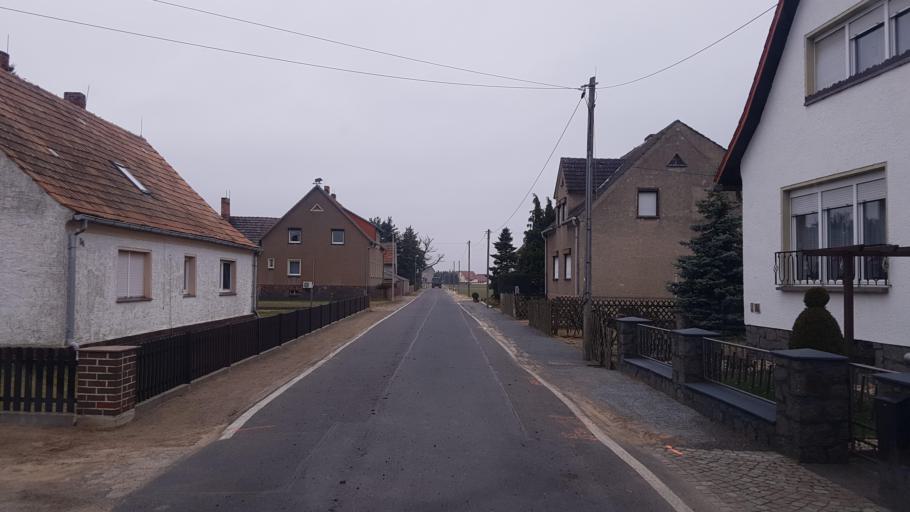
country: DE
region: Brandenburg
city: Herzberg
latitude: 51.6743
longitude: 13.1727
